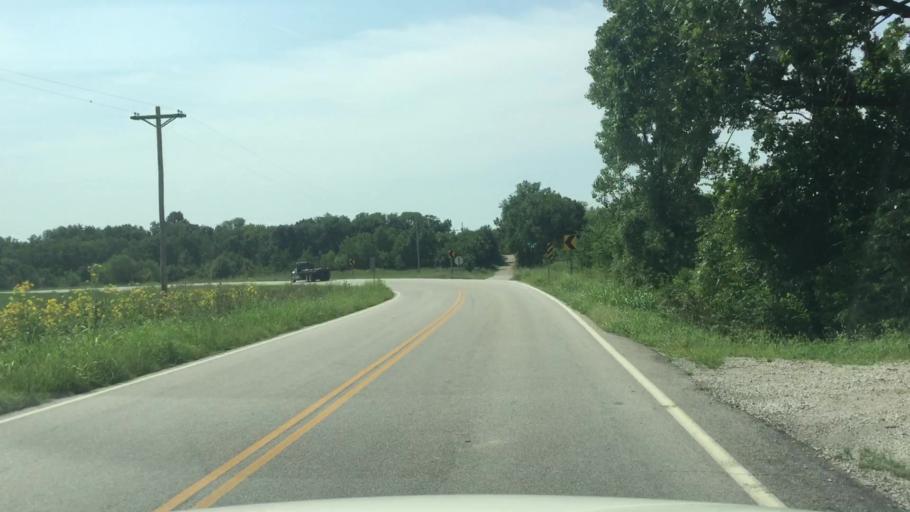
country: US
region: Kansas
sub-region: Montgomery County
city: Cherryvale
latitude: 37.1956
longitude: -95.5581
